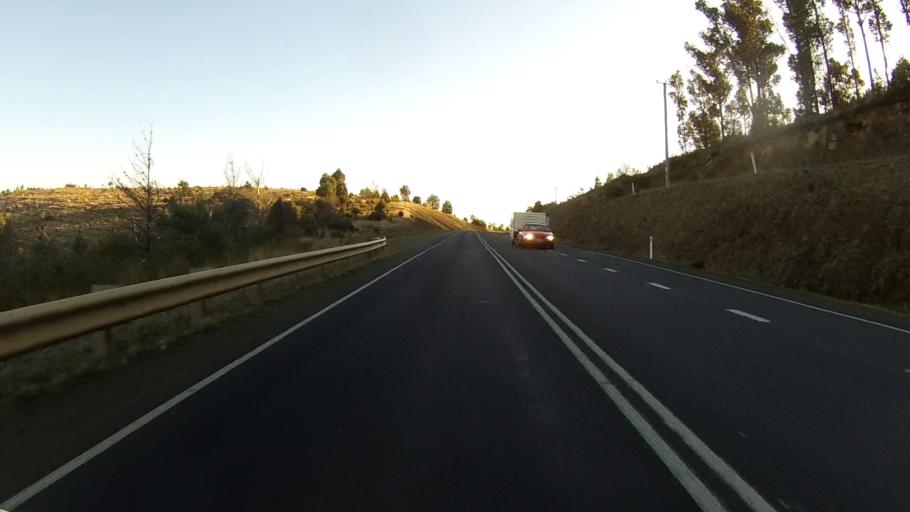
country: AU
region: Tasmania
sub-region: Sorell
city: Sorell
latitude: -42.8239
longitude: 147.7306
